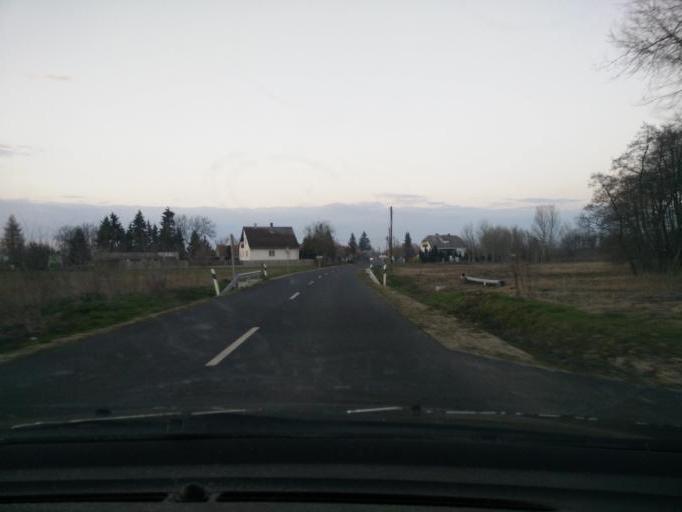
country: HU
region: Veszprem
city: Csabrendek
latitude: 47.0589
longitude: 17.3394
